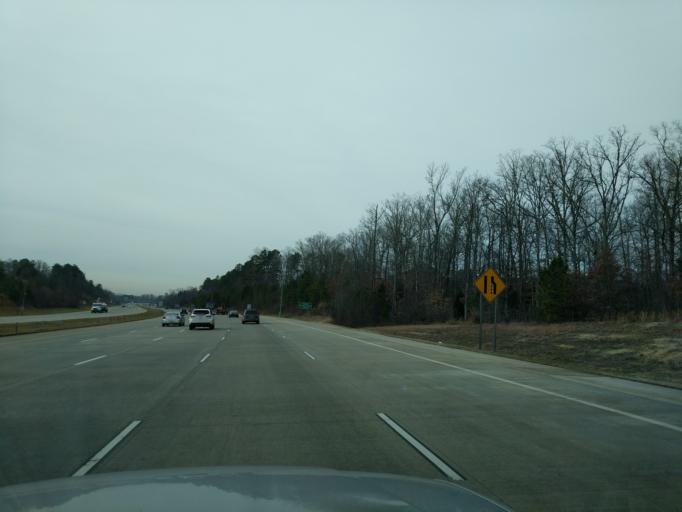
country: US
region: North Carolina
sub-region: Mecklenburg County
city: Huntersville
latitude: 35.3611
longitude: -80.8548
